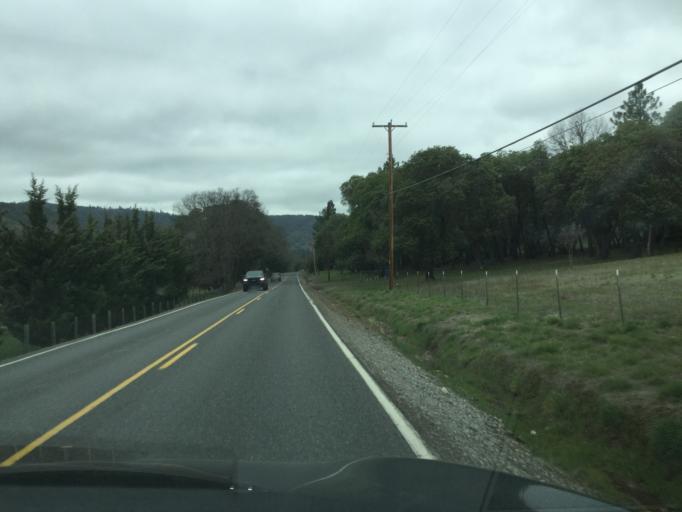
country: US
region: Oregon
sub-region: Jackson County
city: Gold Hill
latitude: 42.3989
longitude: -123.0193
